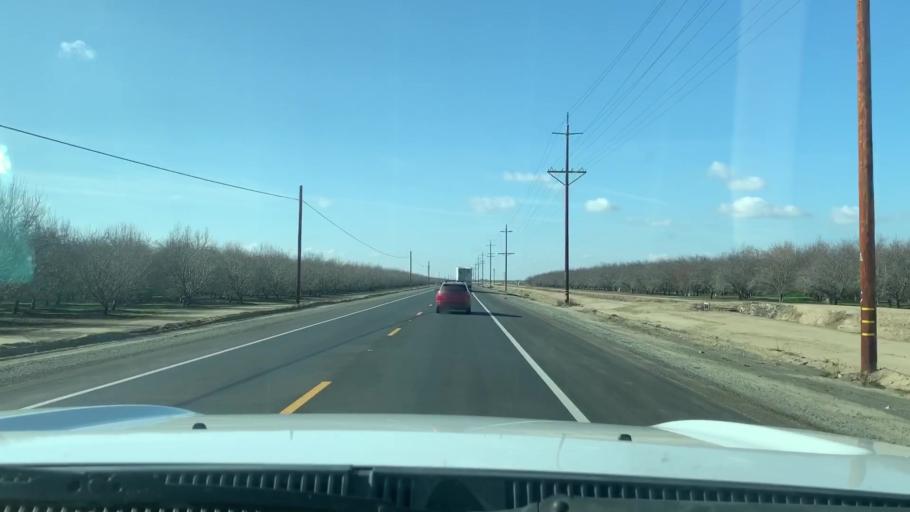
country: US
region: California
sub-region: Kern County
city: Wasco
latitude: 35.6017
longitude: -119.2897
